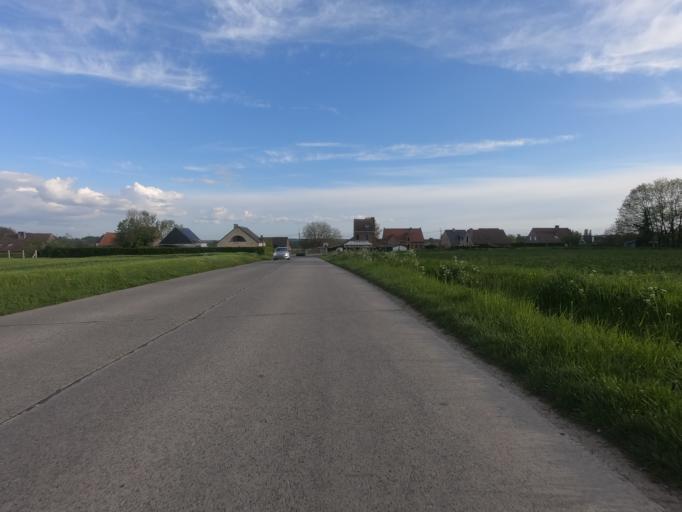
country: BE
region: Flanders
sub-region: Provincie Vlaams-Brabant
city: Galmaarden
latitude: 50.7877
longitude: 3.9798
